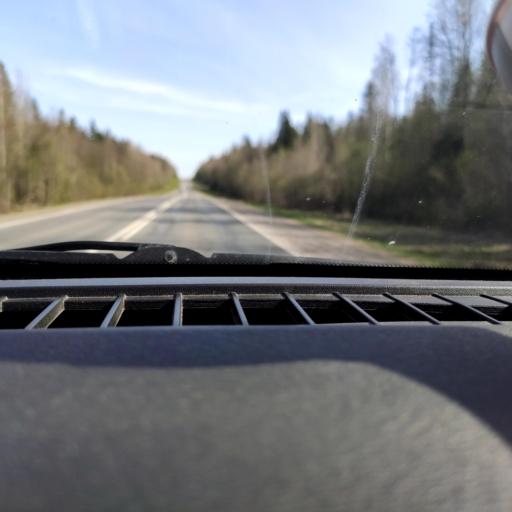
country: RU
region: Perm
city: Perm
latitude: 58.1590
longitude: 56.2476
